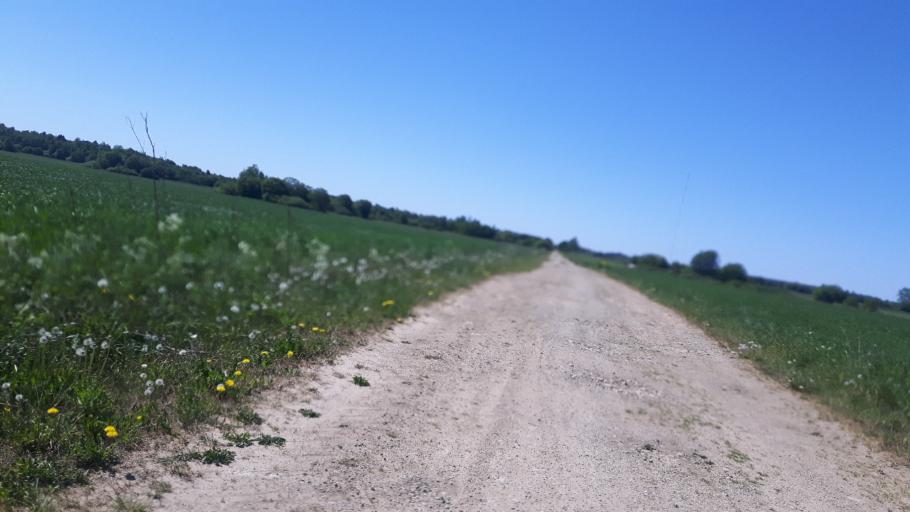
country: EE
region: Ida-Virumaa
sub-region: Toila vald
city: Voka
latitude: 59.4037
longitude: 27.6553
